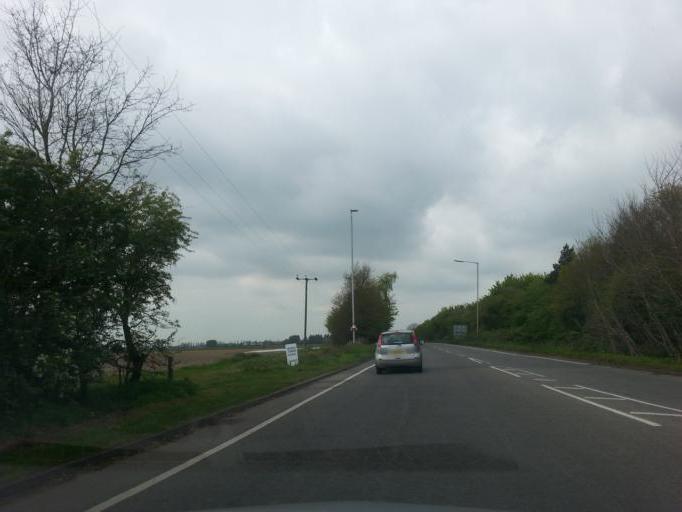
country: GB
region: England
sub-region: Norfolk
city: Outwell
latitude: 52.6192
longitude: 0.2232
